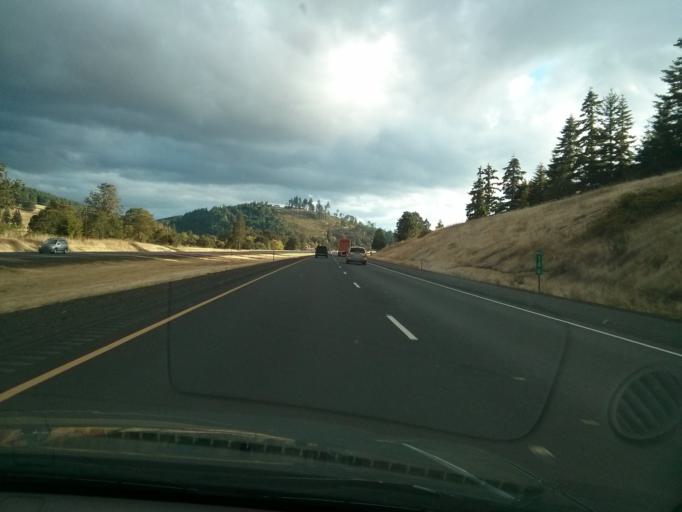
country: US
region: Oregon
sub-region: Douglas County
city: Yoncalla
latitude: 43.5099
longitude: -123.3166
